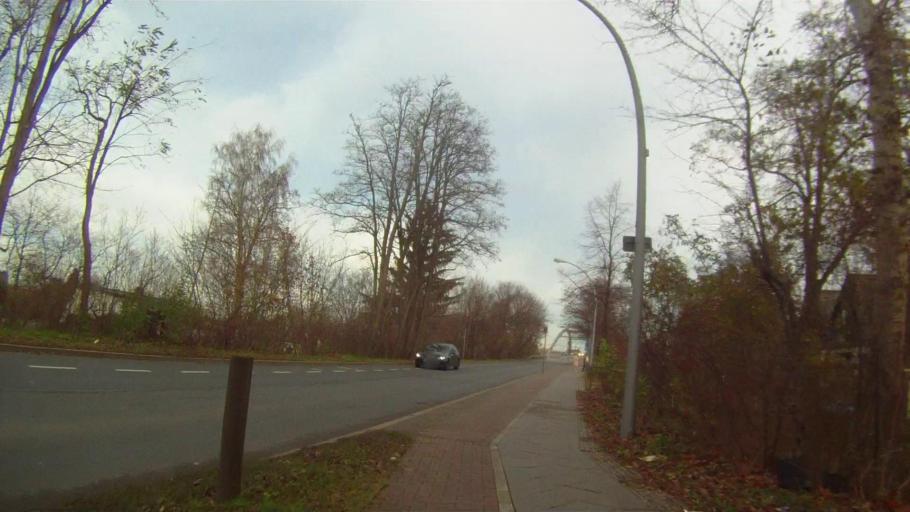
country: DE
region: Berlin
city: Buckow
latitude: 52.4410
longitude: 13.4767
